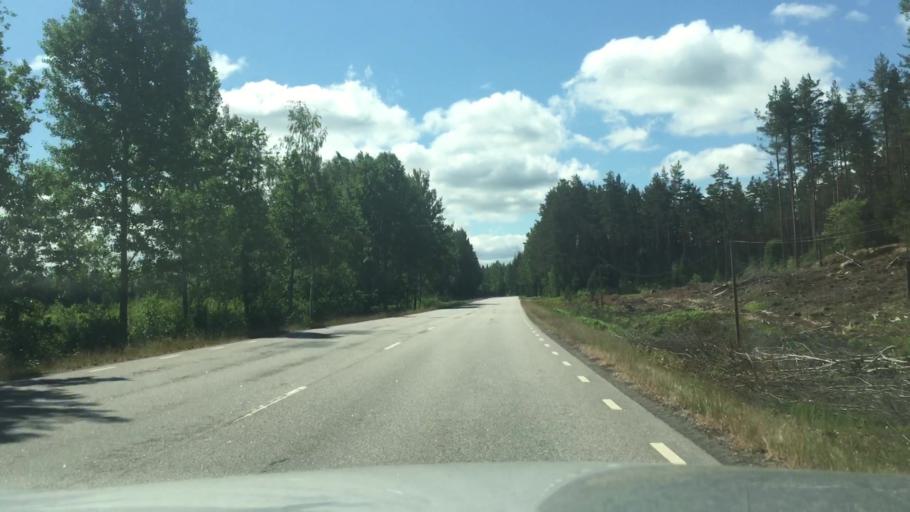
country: SE
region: Vaestra Goetaland
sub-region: Karlsborgs Kommun
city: Molltorp
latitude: 58.6246
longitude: 14.3888
